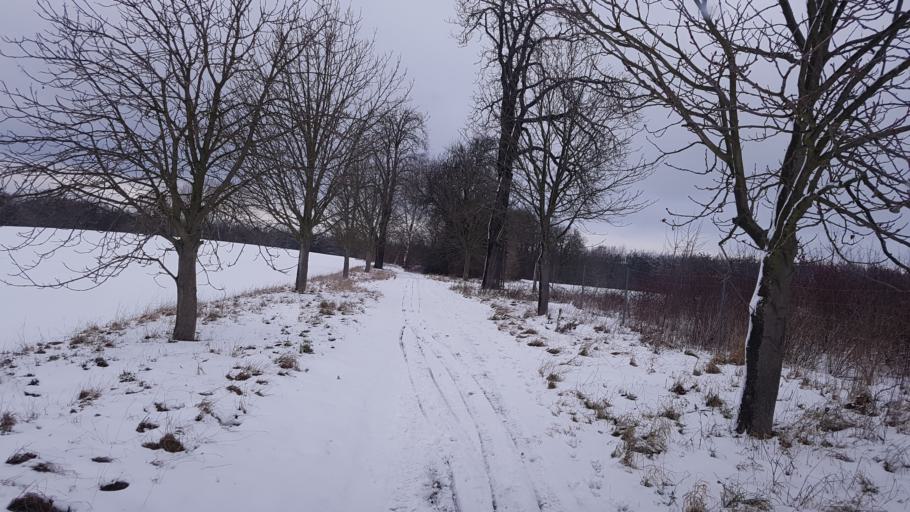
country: DE
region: Brandenburg
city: Crinitz
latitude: 51.7320
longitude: 13.7680
